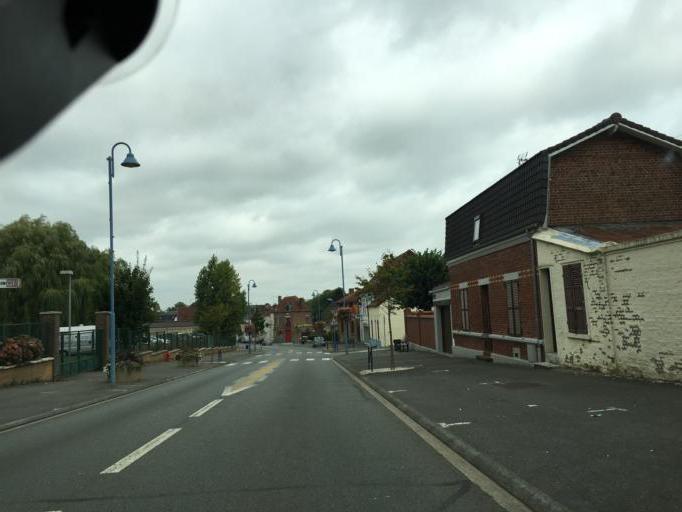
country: FR
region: Nord-Pas-de-Calais
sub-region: Departement du Pas-de-Calais
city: Saint-Pol-sur-Ternoise
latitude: 50.3757
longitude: 2.3332
